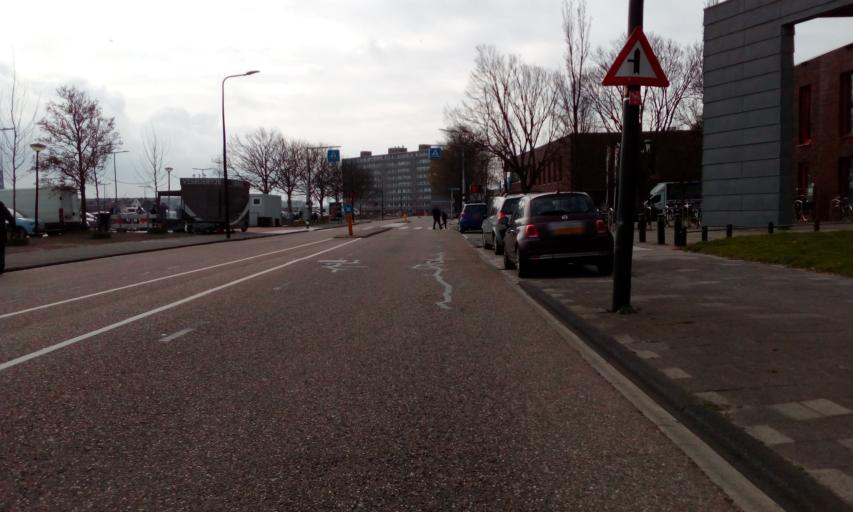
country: NL
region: South Holland
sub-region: Gemeente Maassluis
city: Maassluis
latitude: 51.9289
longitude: 4.2382
